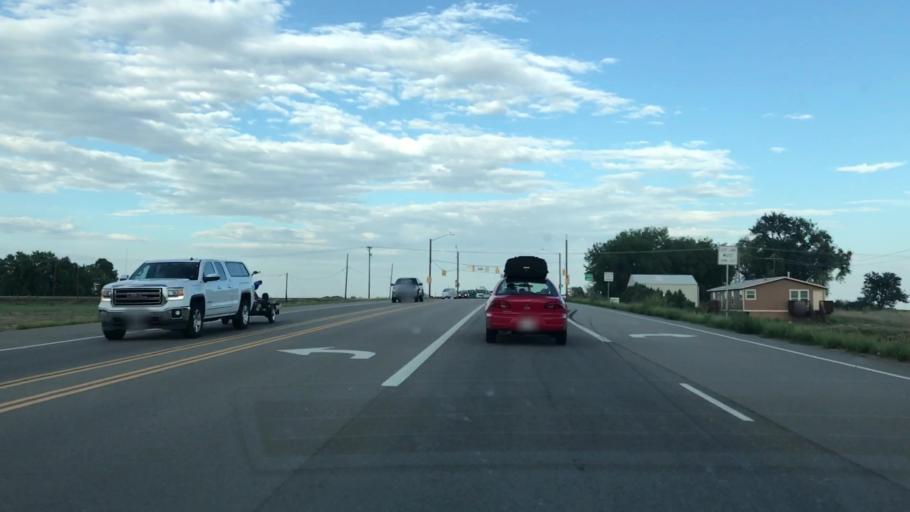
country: US
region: Colorado
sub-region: Weld County
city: Mead
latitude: 40.2044
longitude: -105.0004
